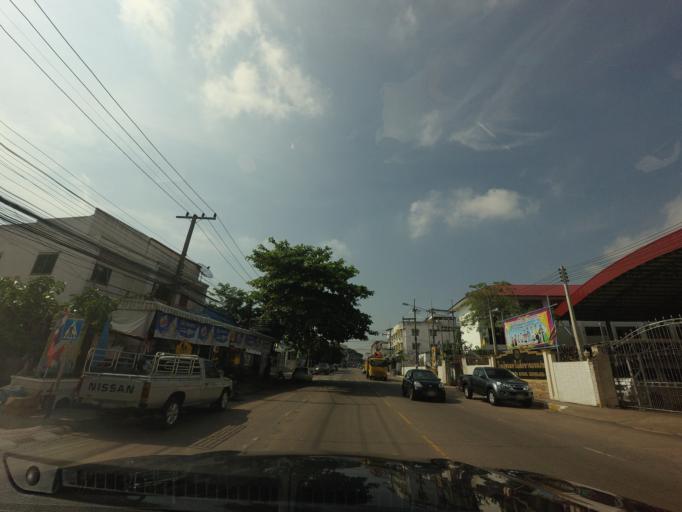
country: TH
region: Khon Kaen
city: Khon Kaen
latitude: 16.4274
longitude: 102.8513
